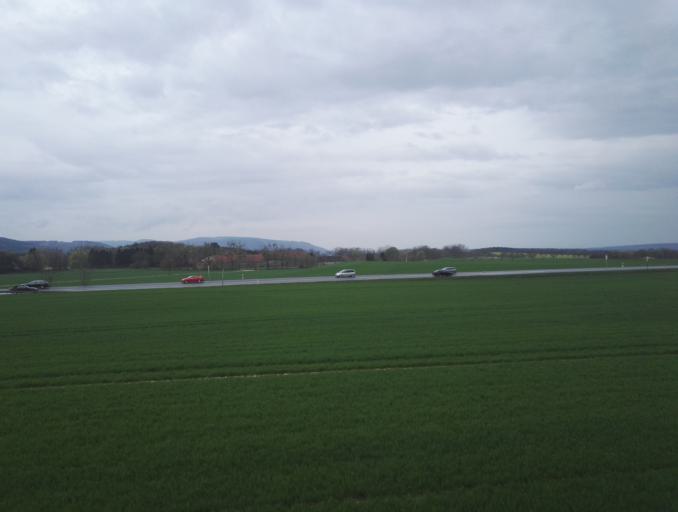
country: DE
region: Lower Saxony
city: Goslar
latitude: 51.9236
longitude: 10.4119
